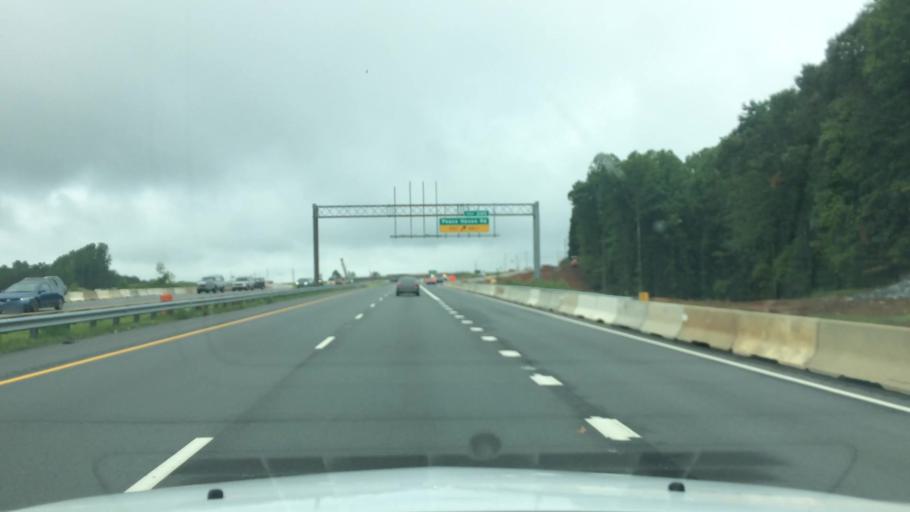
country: US
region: North Carolina
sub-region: Forsyth County
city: Clemmons
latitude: 36.0729
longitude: -80.3524
